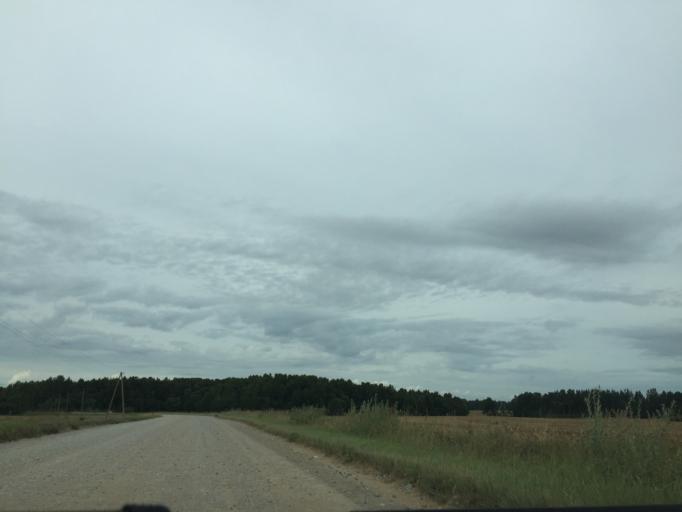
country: LV
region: Dobeles Rajons
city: Dobele
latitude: 56.7100
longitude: 23.1819
